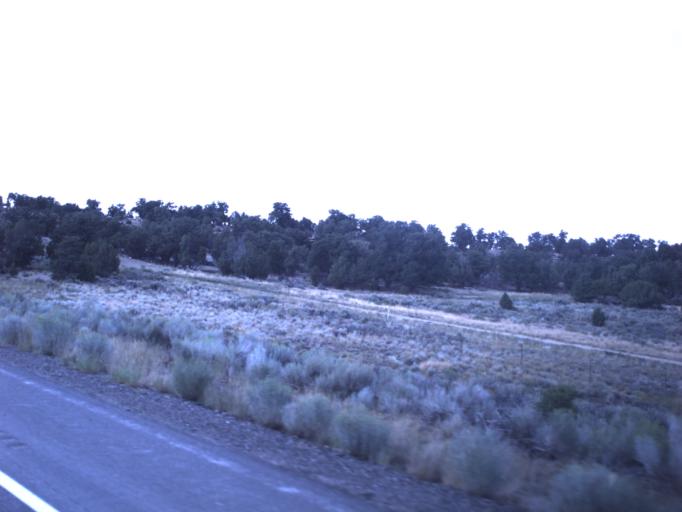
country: US
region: Utah
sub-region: Duchesne County
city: Duchesne
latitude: 40.1774
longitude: -110.5972
